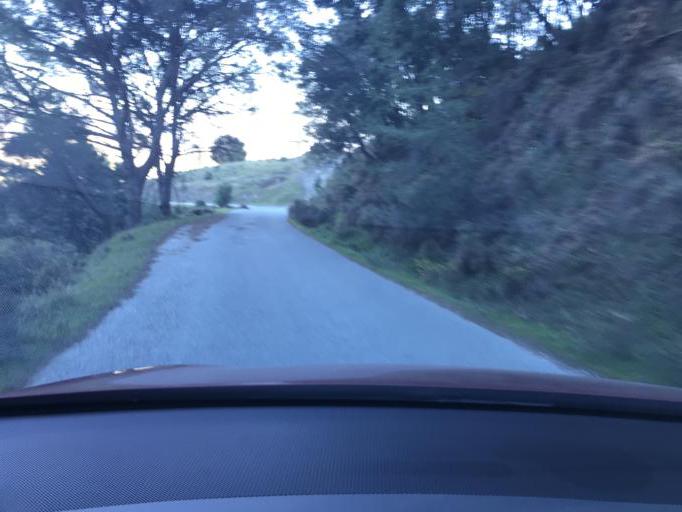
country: ES
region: Andalusia
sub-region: Provincia de Malaga
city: Tolox
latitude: 36.6814
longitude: -4.9154
